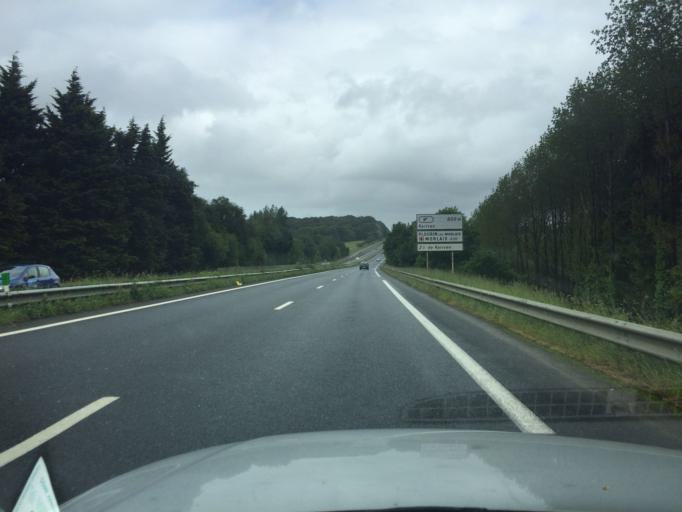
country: FR
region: Brittany
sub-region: Departement du Finistere
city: Morlaix
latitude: 48.5597
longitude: -3.8684
